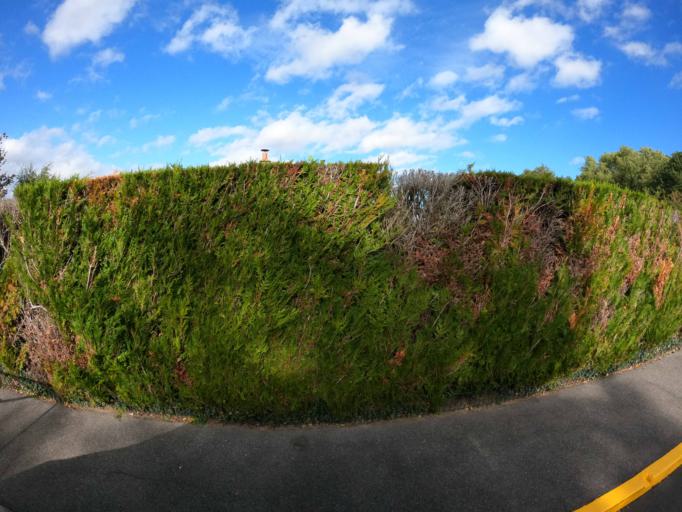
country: FR
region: Ile-de-France
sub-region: Departement de Seine-et-Marne
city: Esbly
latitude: 48.8941
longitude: 2.8138
